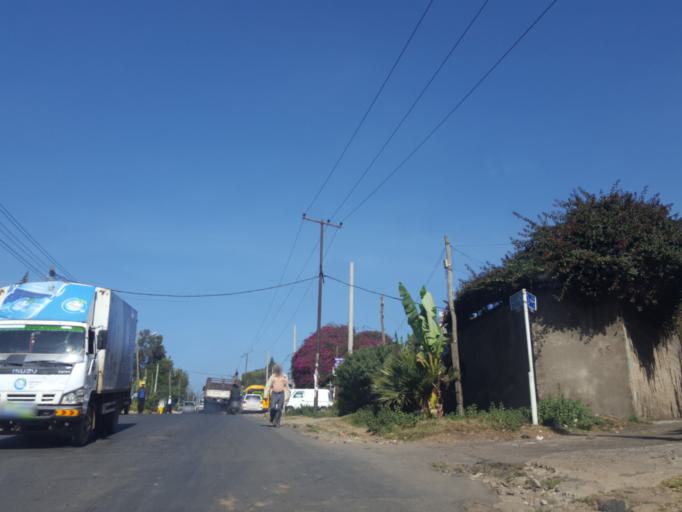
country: ET
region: Adis Abeba
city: Addis Ababa
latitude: 9.0513
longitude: 38.7371
